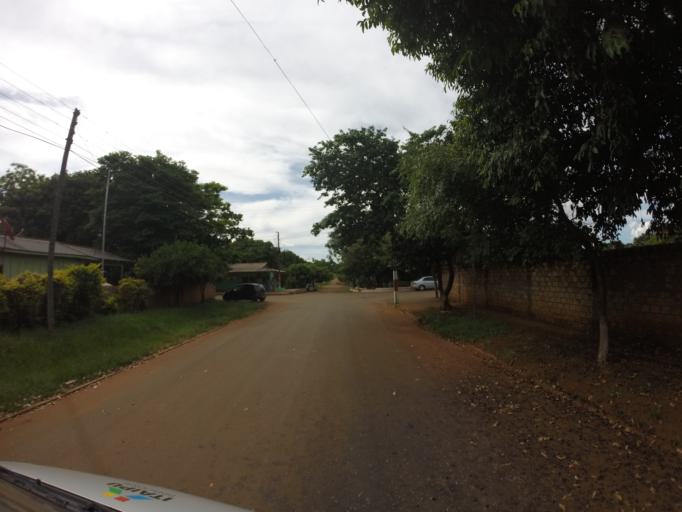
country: PY
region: Alto Parana
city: Ciudad del Este
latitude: -25.4346
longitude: -54.6415
